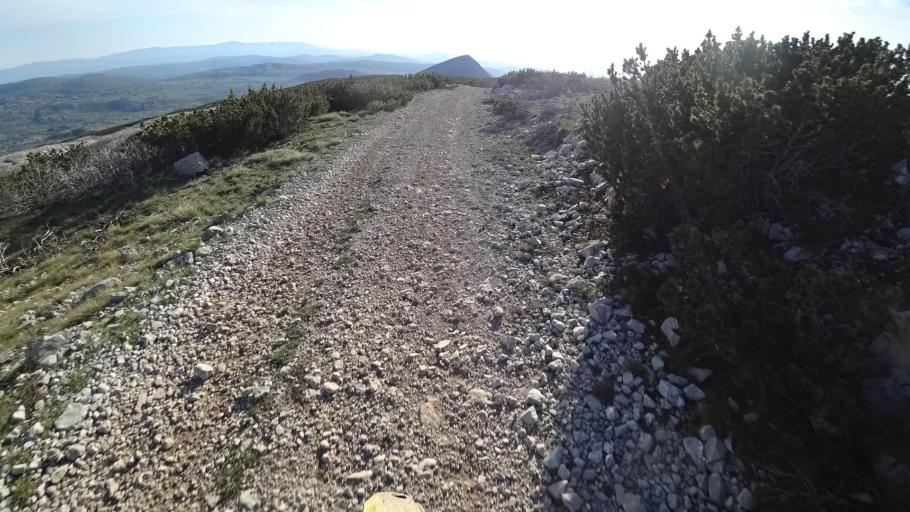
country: BA
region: Federation of Bosnia and Herzegovina
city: Kocerin
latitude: 43.5920
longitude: 17.5398
